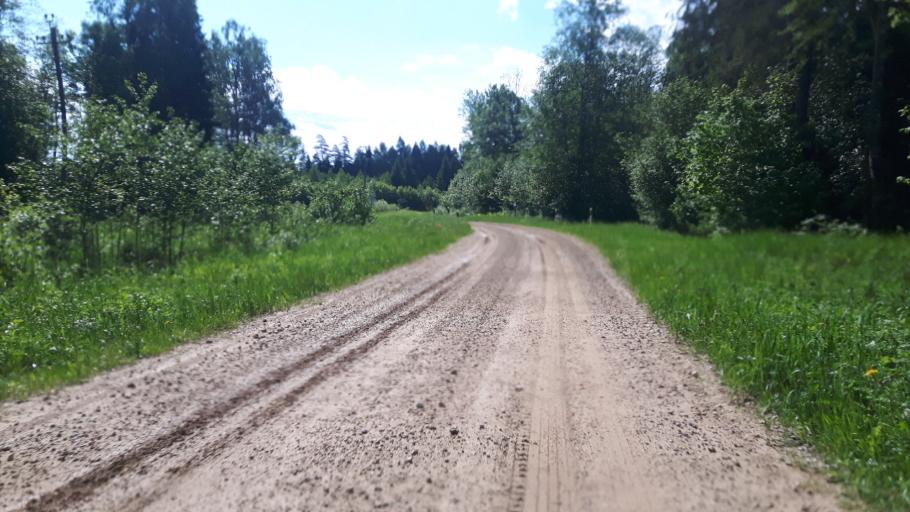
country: EE
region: Paernumaa
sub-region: Vaendra vald (alev)
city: Vandra
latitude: 58.7109
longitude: 25.0443
